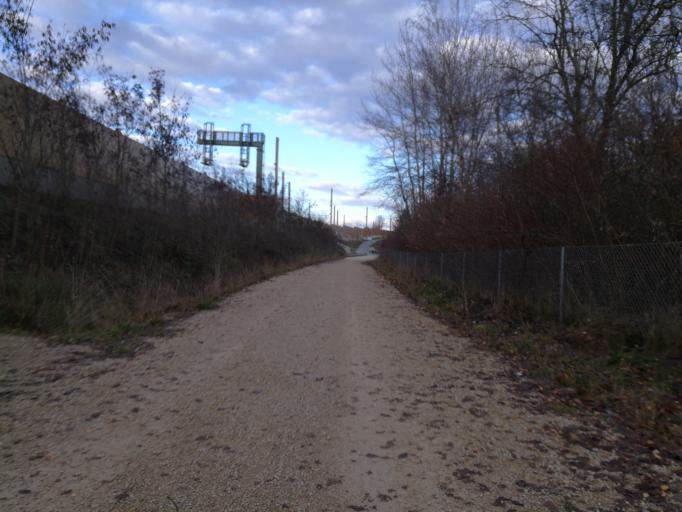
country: DE
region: Bavaria
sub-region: Regierungsbezirk Mittelfranken
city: Furth
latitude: 49.4911
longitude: 10.9674
